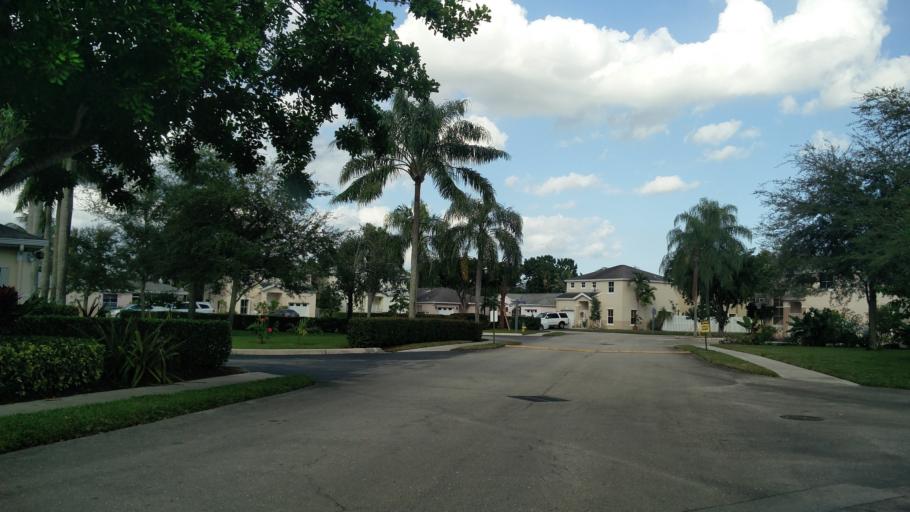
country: US
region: Florida
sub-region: Broward County
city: Davie
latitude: 26.0691
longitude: -80.2428
